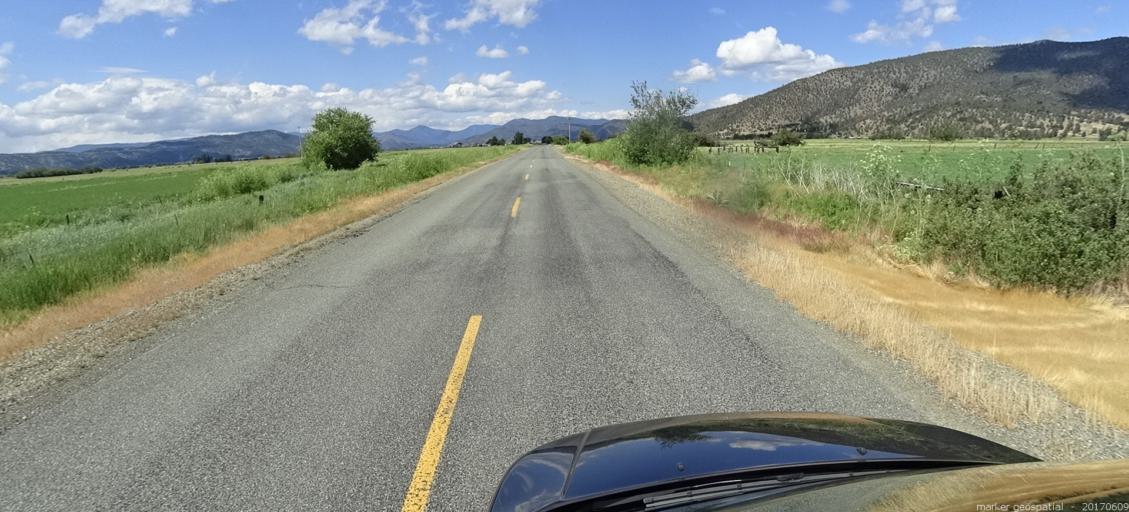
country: US
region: California
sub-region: Siskiyou County
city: Yreka
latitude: 41.5031
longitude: -122.8581
